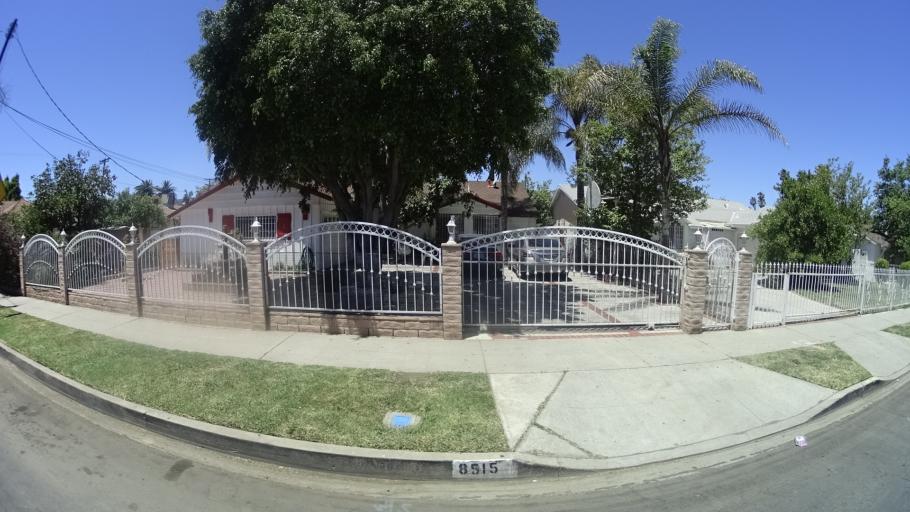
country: US
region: California
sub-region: Los Angeles County
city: Van Nuys
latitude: 34.2253
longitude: -118.4699
